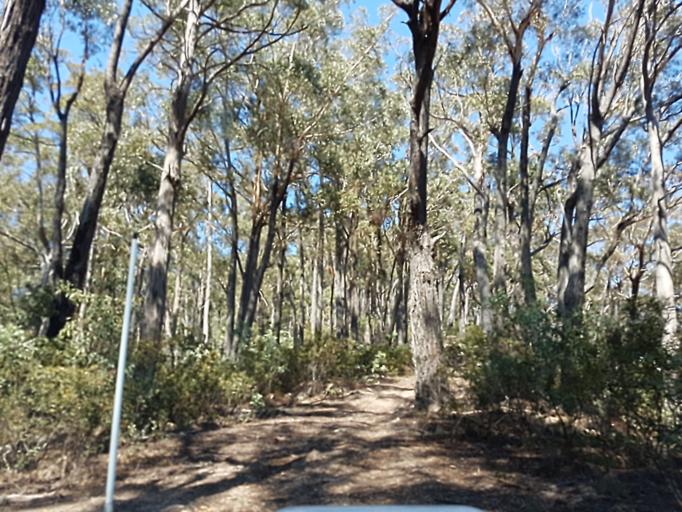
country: AU
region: Victoria
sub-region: East Gippsland
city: Lakes Entrance
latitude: -37.2876
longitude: 148.3285
